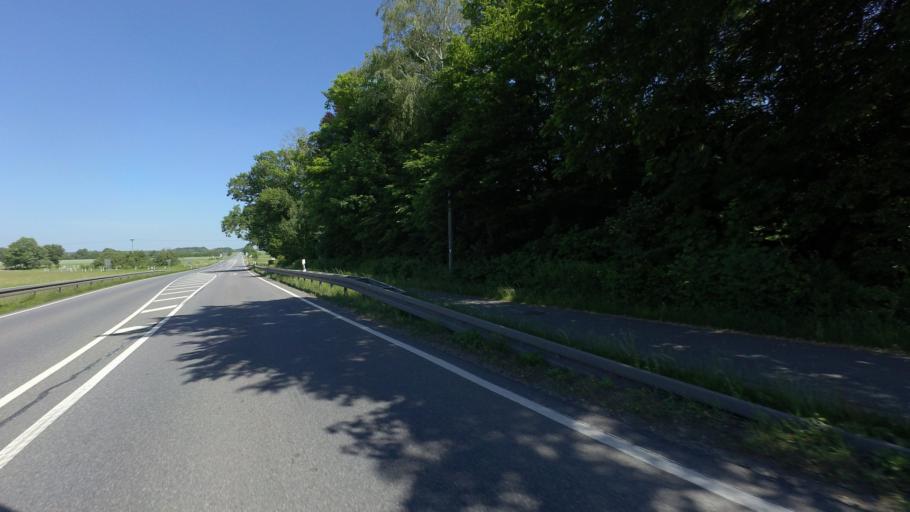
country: DE
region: Brandenburg
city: Spremberg
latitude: 51.6578
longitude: 14.3602
